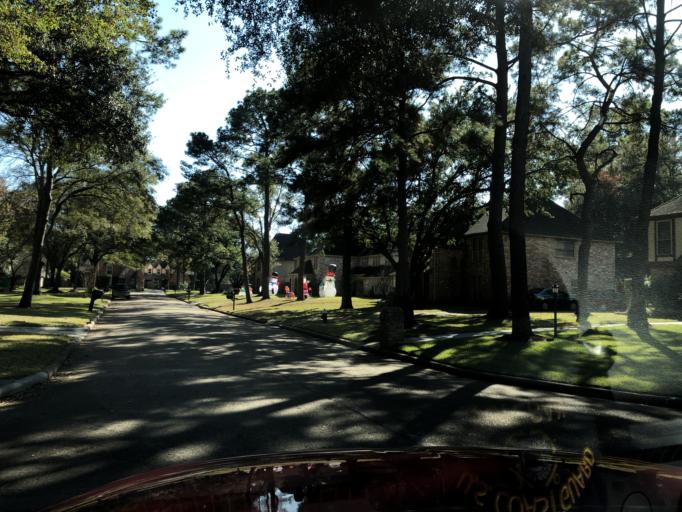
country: US
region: Texas
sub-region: Harris County
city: Tomball
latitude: 30.0281
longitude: -95.5414
